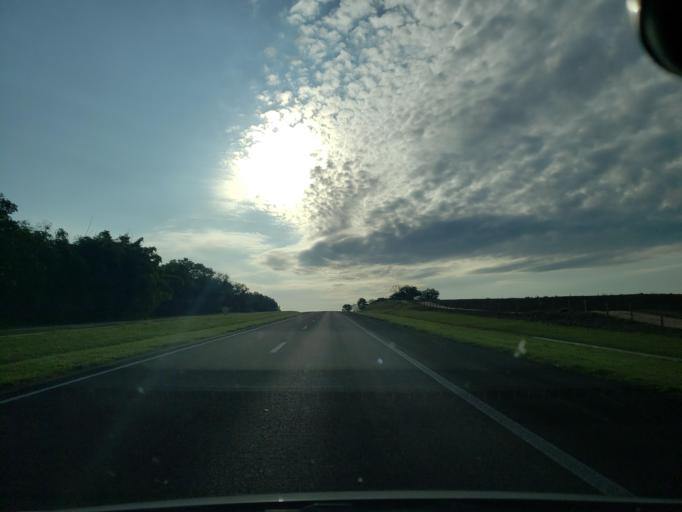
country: BR
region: Sao Paulo
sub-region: Valparaiso
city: Valparaiso
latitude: -21.1847
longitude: -50.9158
